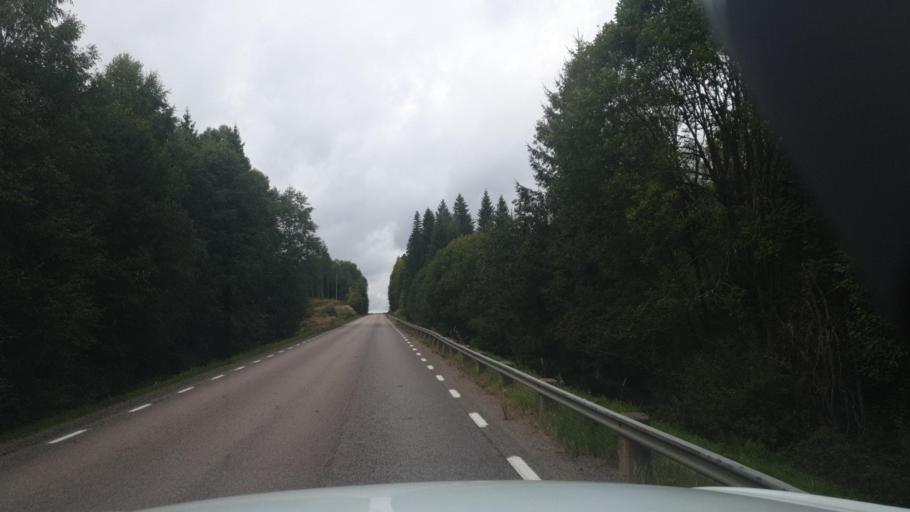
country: SE
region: Vaermland
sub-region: Torsby Kommun
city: Torsby
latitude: 59.9240
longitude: 12.8657
